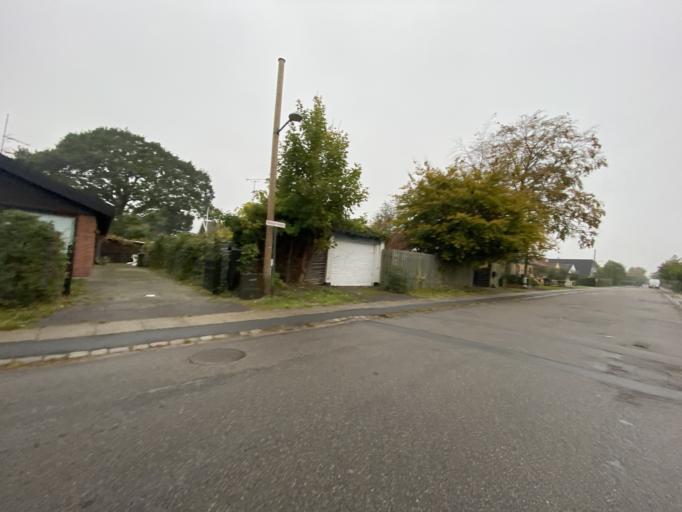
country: DK
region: Capital Region
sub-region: Dragor Kommune
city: Dragor
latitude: 55.5859
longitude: 12.6507
